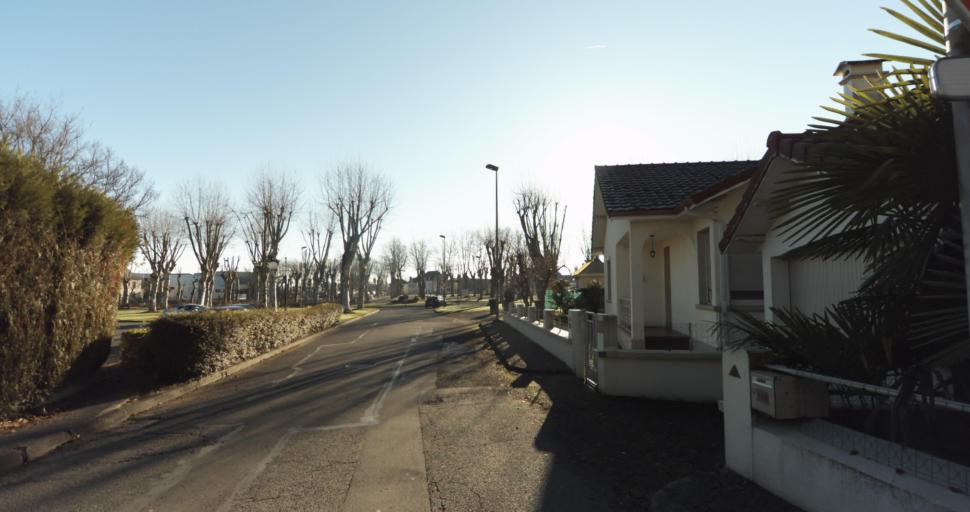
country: FR
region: Aquitaine
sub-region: Departement des Pyrenees-Atlantiques
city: Morlaas
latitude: 43.3416
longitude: -0.2659
